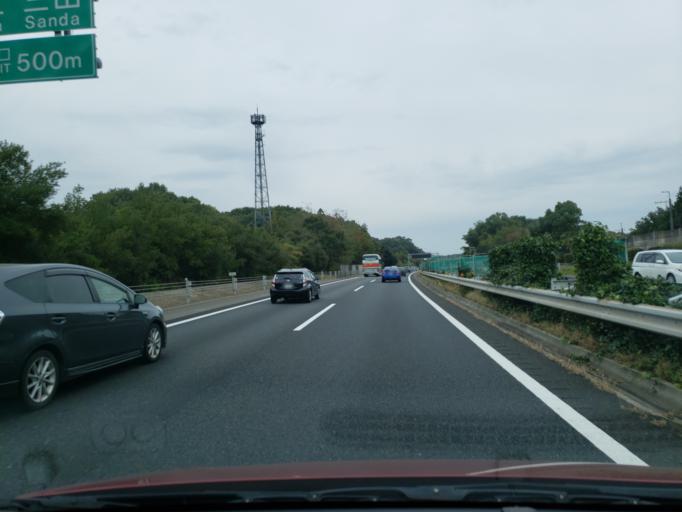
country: JP
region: Hyogo
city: Sandacho
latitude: 34.8370
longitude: 135.1915
